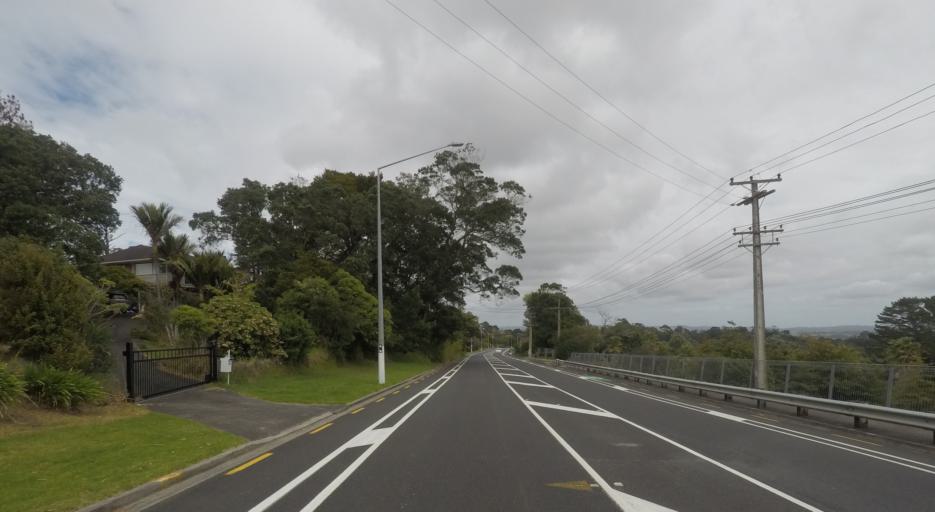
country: NZ
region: Auckland
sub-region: Auckland
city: North Shore
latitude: -36.7740
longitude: 174.6929
